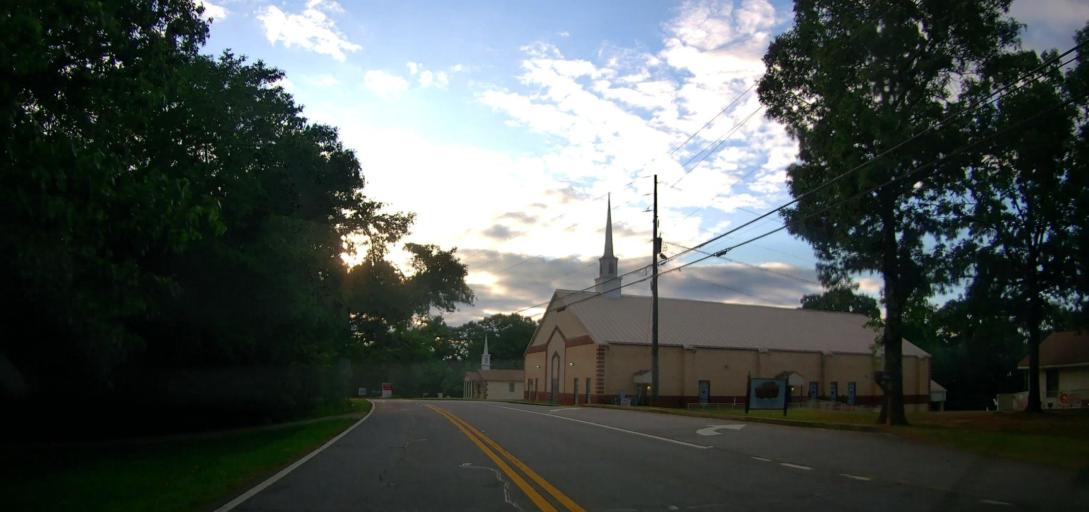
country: US
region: Georgia
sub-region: Clarke County
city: Athens
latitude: 33.9192
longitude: -83.4034
